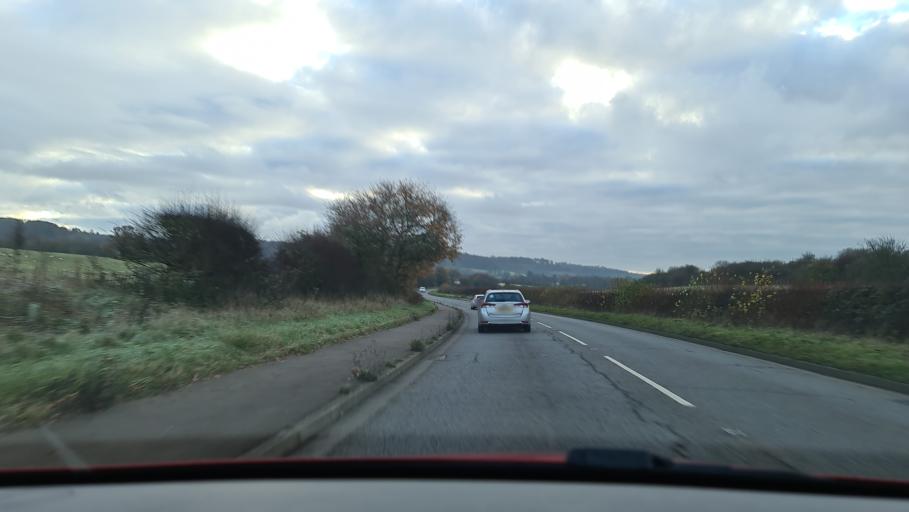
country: GB
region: England
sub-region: Buckinghamshire
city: Princes Risborough
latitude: 51.6725
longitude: -0.8187
